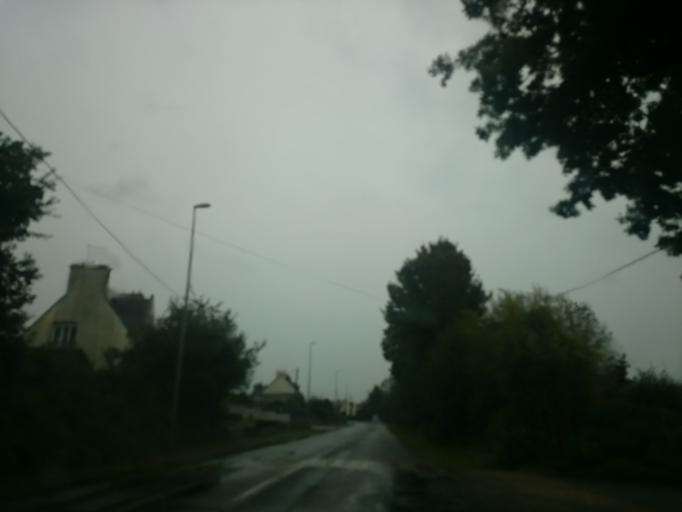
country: FR
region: Brittany
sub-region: Departement du Finistere
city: Le Drennec
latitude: 48.5308
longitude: -4.3760
